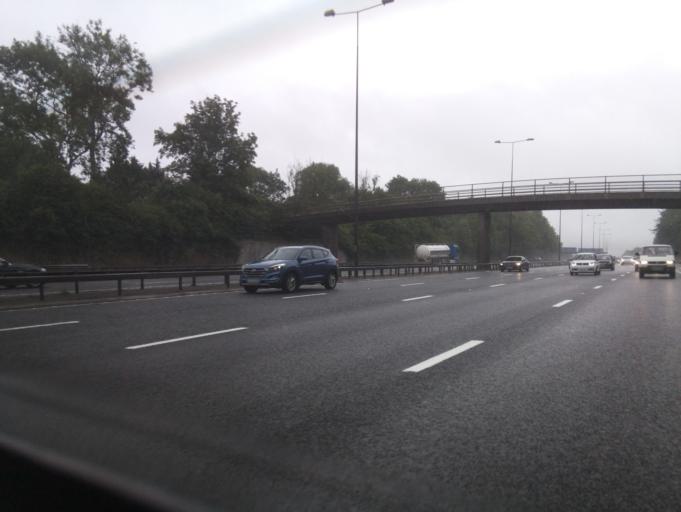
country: GB
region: England
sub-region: Surrey
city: Reigate
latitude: 51.2572
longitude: -0.2063
